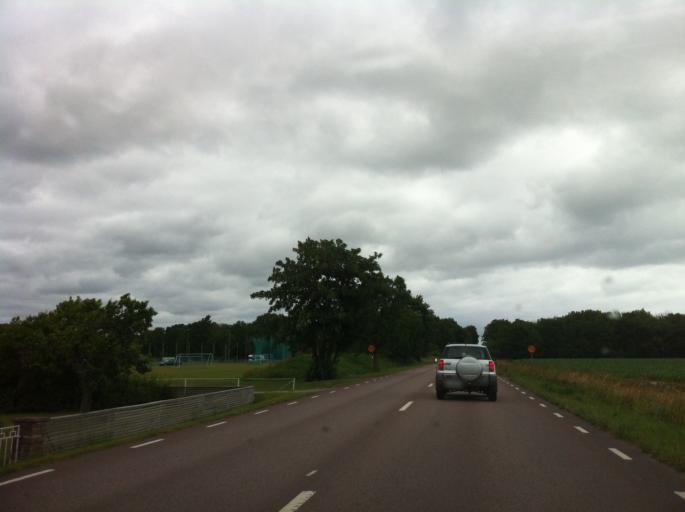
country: SE
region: Kalmar
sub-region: Borgholms Kommun
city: Borgholm
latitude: 57.1658
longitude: 17.0152
